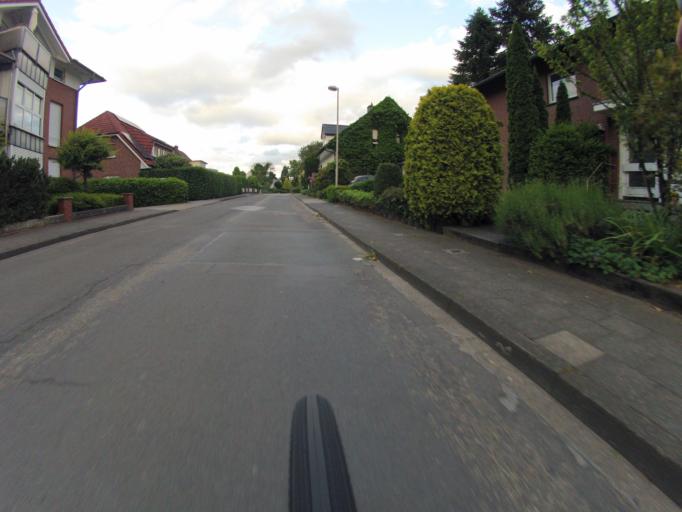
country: DE
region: North Rhine-Westphalia
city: Ibbenburen
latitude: 52.2782
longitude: 7.7083
